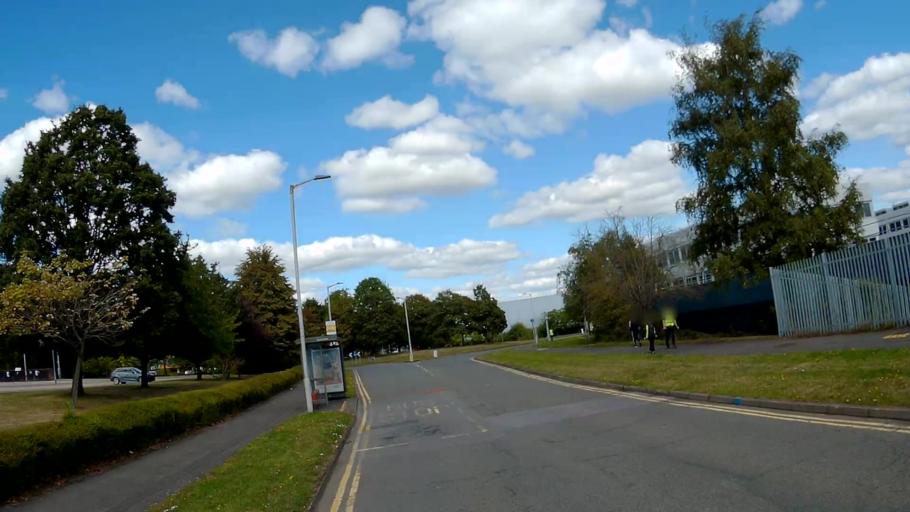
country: GB
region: England
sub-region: Bracknell Forest
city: Bracknell
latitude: 51.4078
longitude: -0.7745
